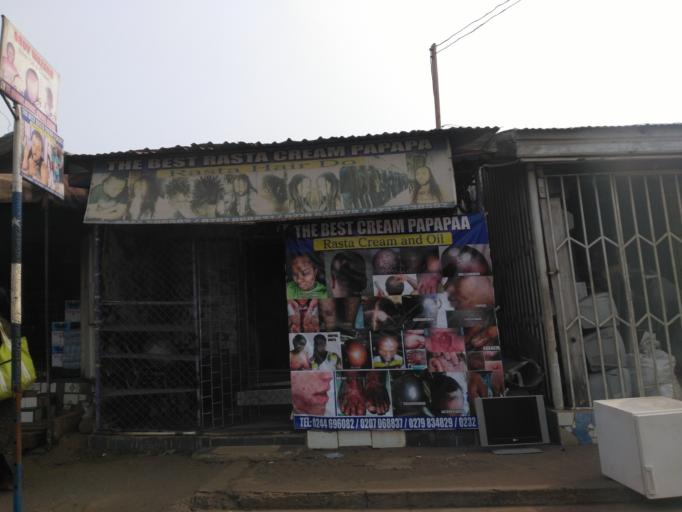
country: GH
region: Ashanti
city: Kumasi
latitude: 6.7056
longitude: -1.6233
